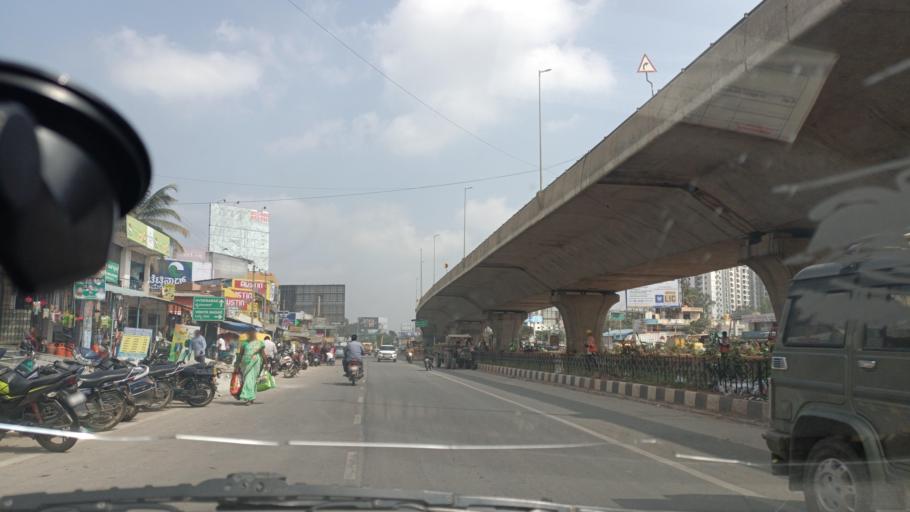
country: IN
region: Karnataka
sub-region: Bangalore Urban
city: Yelahanka
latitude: 13.1604
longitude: 77.6259
